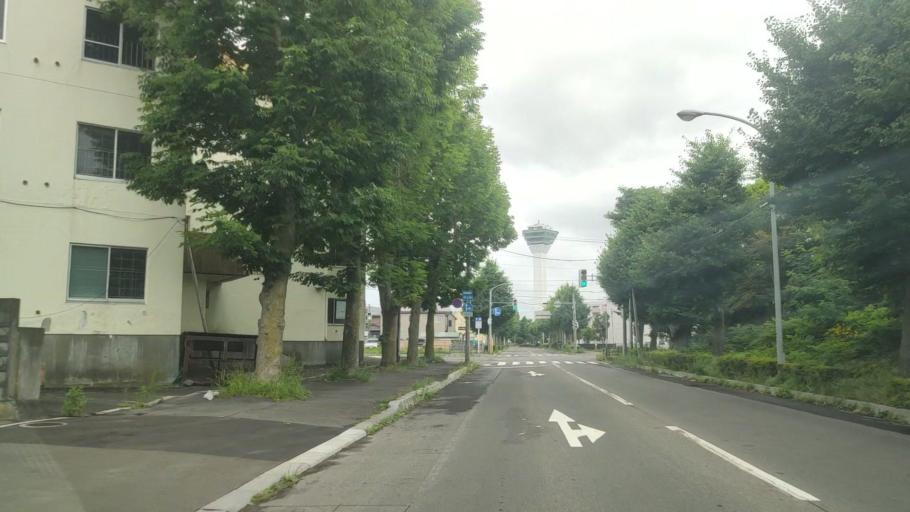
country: JP
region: Hokkaido
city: Hakodate
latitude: 41.7938
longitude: 140.7606
